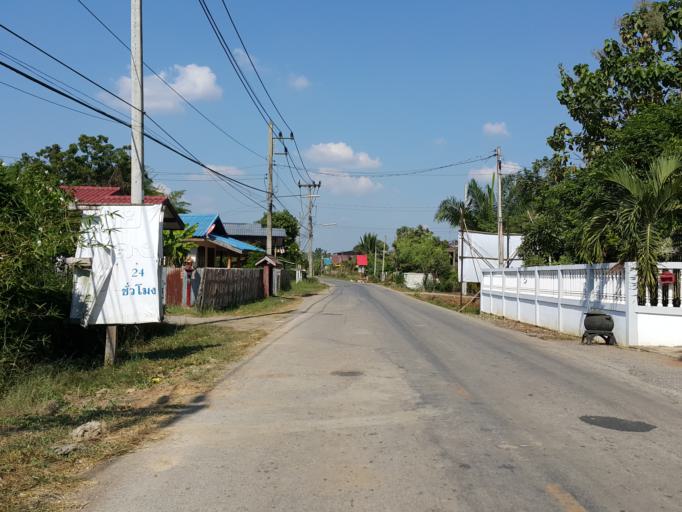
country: TH
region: Sukhothai
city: Thung Saliam
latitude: 17.3245
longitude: 99.5497
